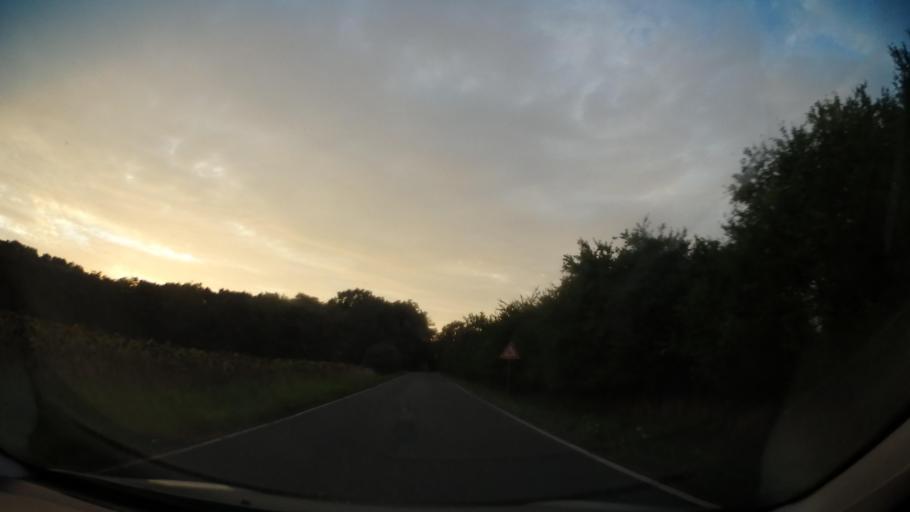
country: CZ
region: Central Bohemia
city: Loucen
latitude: 50.2636
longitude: 15.0212
